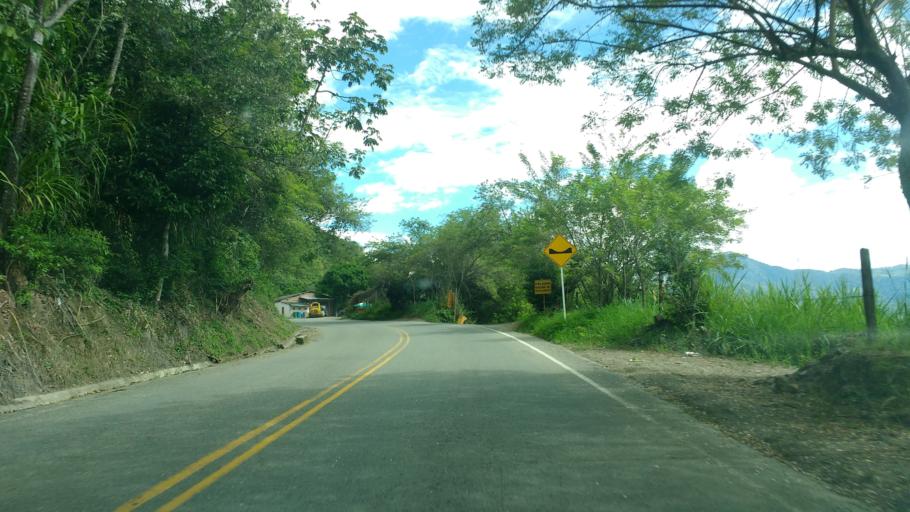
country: CO
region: Antioquia
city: Titiribi
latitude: 6.0242
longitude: -75.7655
